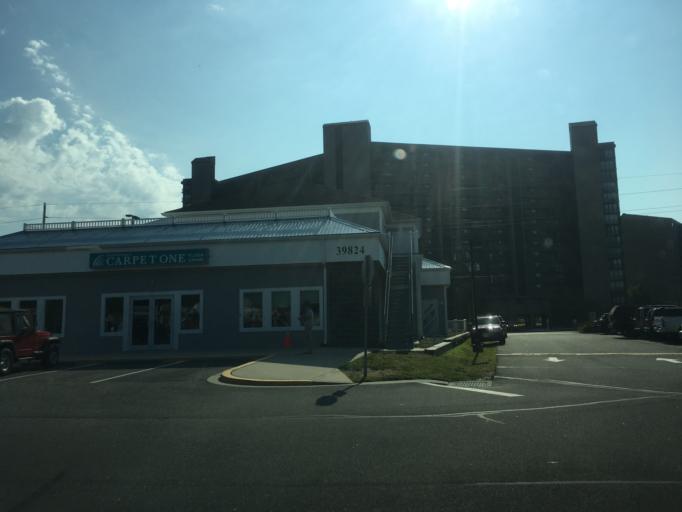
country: US
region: Delaware
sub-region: Sussex County
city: Bethany Beach
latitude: 38.5282
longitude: -75.0570
